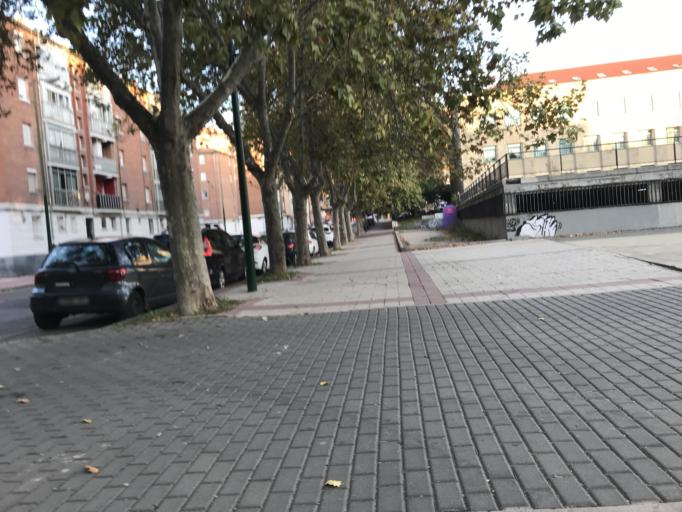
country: ES
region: Castille and Leon
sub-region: Provincia de Valladolid
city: Valladolid
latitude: 41.6577
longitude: -4.7142
